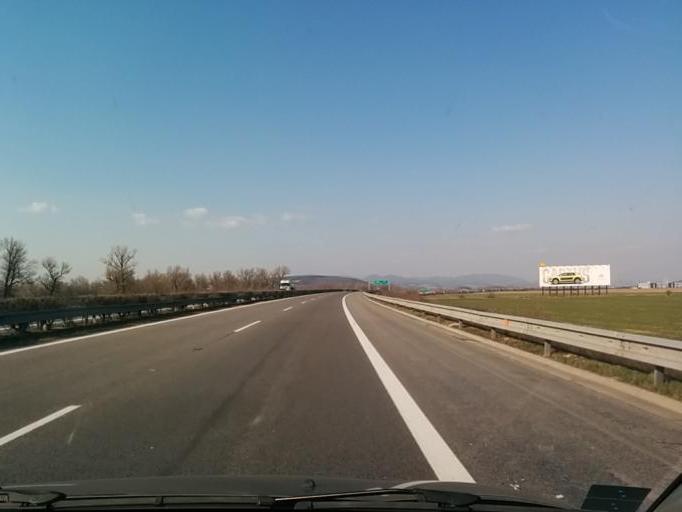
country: SK
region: Trenciansky
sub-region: Okres Nove Mesto nad Vahom
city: Nove Mesto nad Vahom
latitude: 48.7450
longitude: 17.8601
